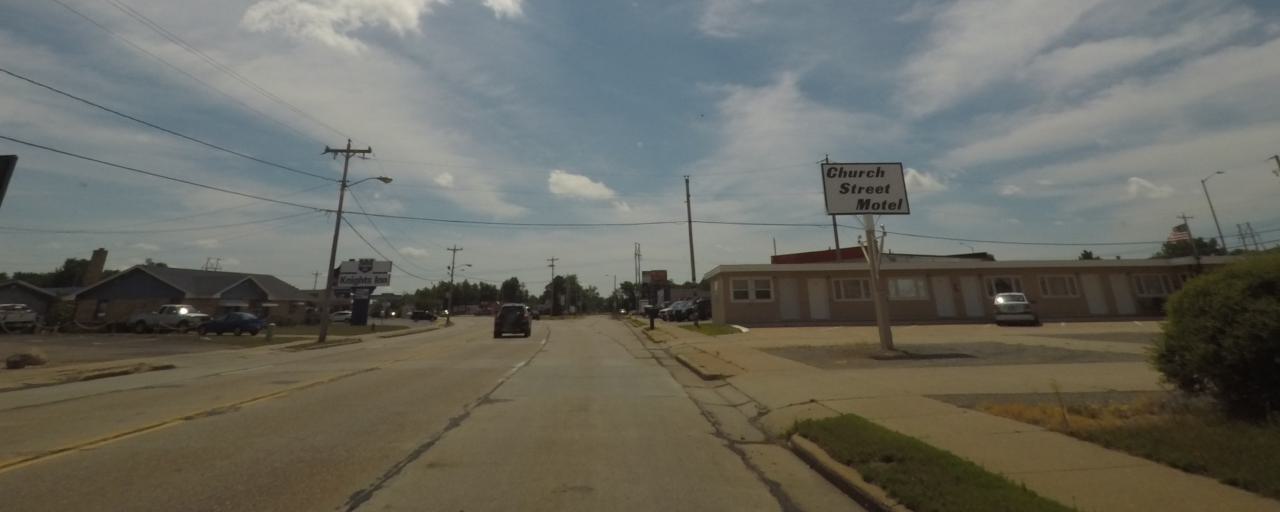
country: US
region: Wisconsin
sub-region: Portage County
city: Whiting
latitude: 44.4996
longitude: -89.5631
